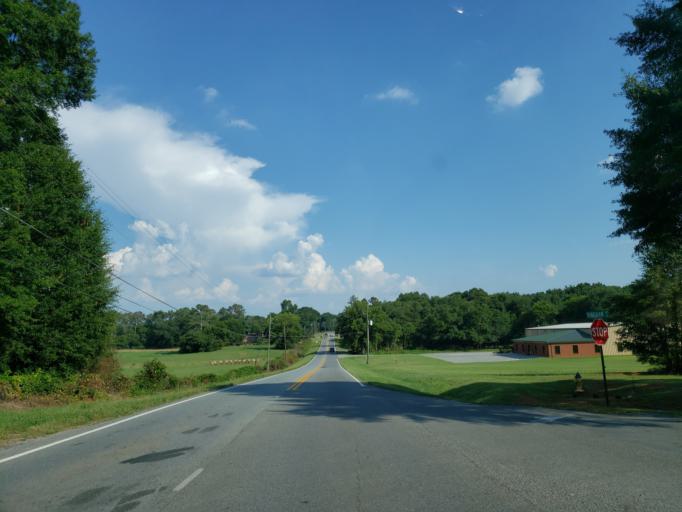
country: US
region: Georgia
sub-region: Bartow County
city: Cartersville
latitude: 34.2008
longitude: -84.8401
